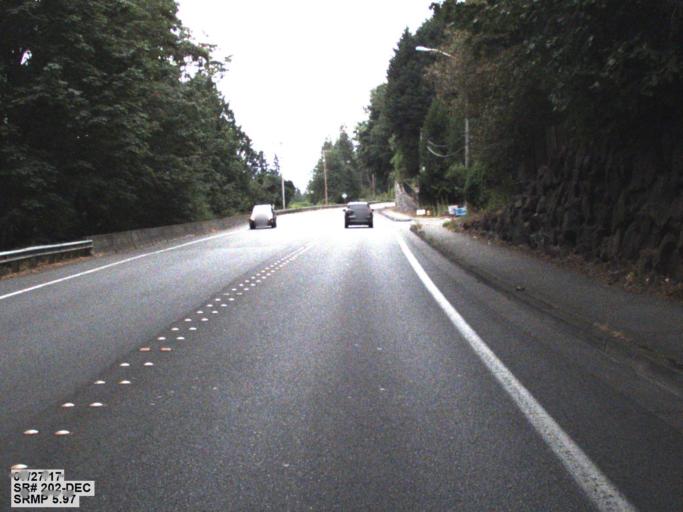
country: US
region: Washington
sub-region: King County
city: Redmond
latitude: 47.6871
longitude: -122.1280
